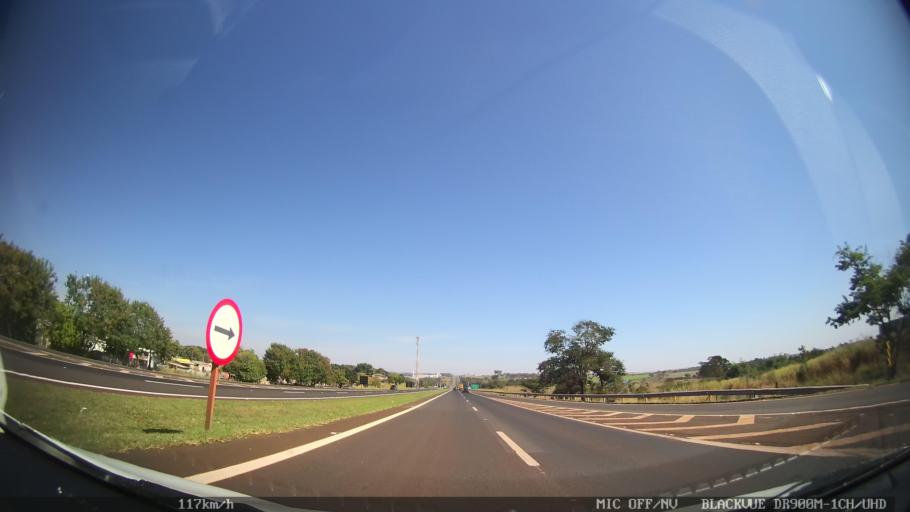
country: BR
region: Sao Paulo
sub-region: Ribeirao Preto
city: Ribeirao Preto
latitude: -21.1022
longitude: -47.8026
